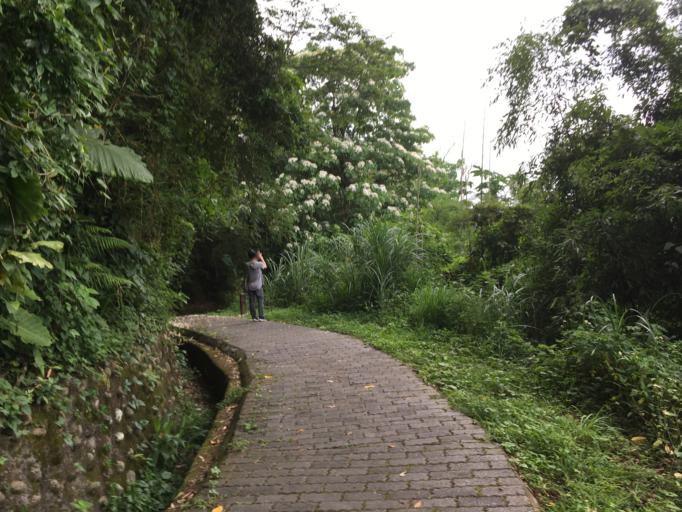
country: TW
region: Taiwan
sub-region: Hsinchu
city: Hsinchu
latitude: 24.7516
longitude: 121.0463
